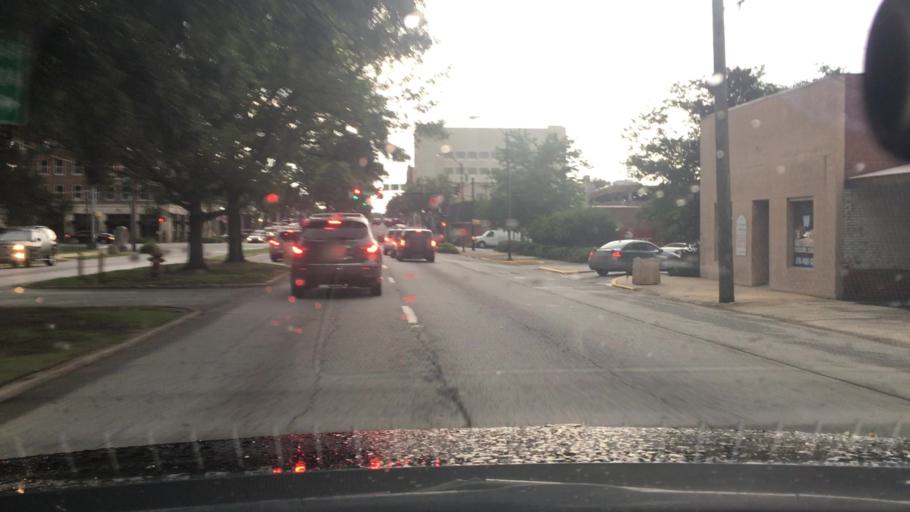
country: US
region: Georgia
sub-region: Spalding County
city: Griffin
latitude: 33.2417
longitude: -84.2514
